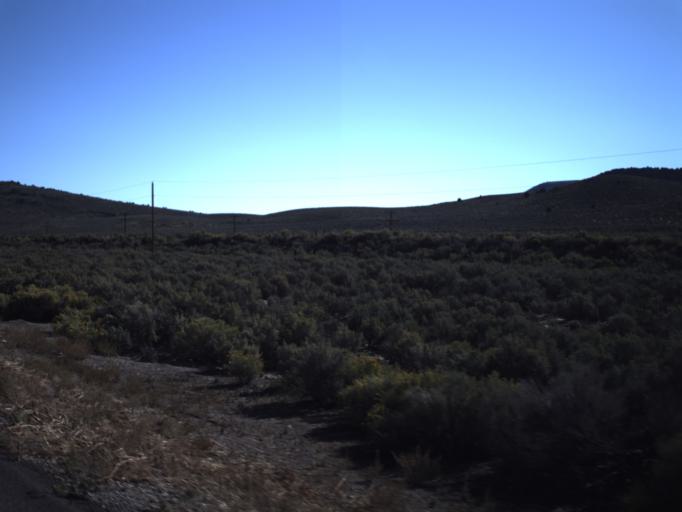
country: US
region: Utah
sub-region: Washington County
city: Enterprise
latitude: 37.7687
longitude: -113.9794
